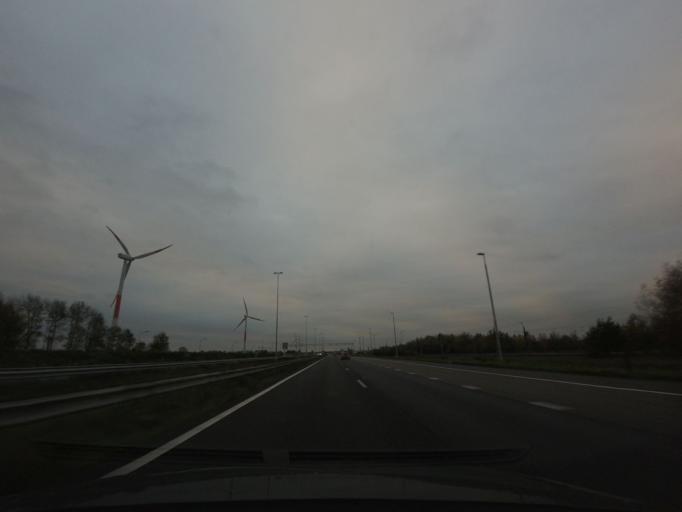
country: NL
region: North Brabant
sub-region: Gemeente Zundert
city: Zundert
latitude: 51.4881
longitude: 4.7364
